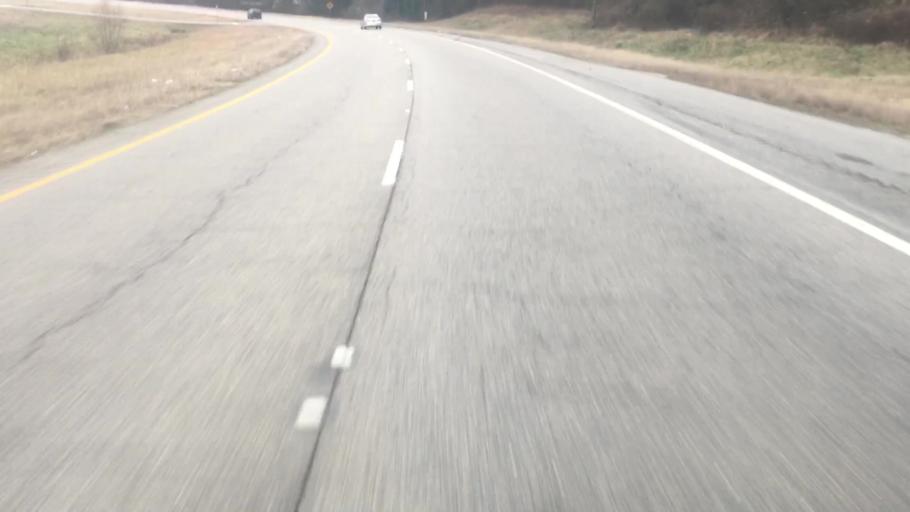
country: US
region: Alabama
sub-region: Walker County
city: Cordova
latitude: 33.8091
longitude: -87.1467
